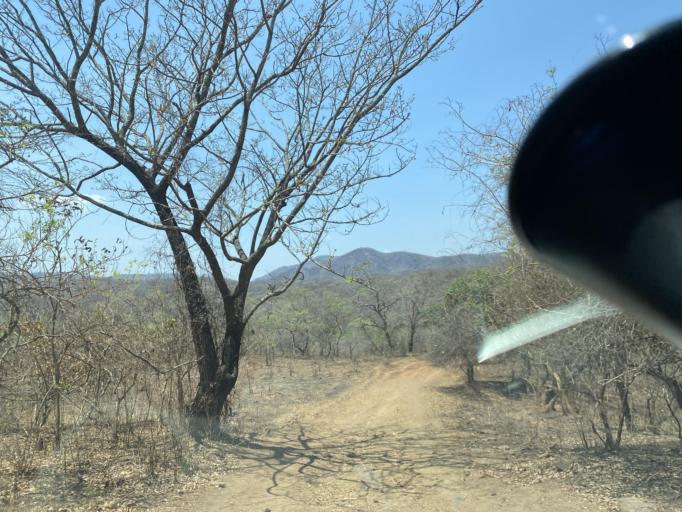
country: ZM
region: Lusaka
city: Kafue
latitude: -15.7877
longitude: 28.4590
